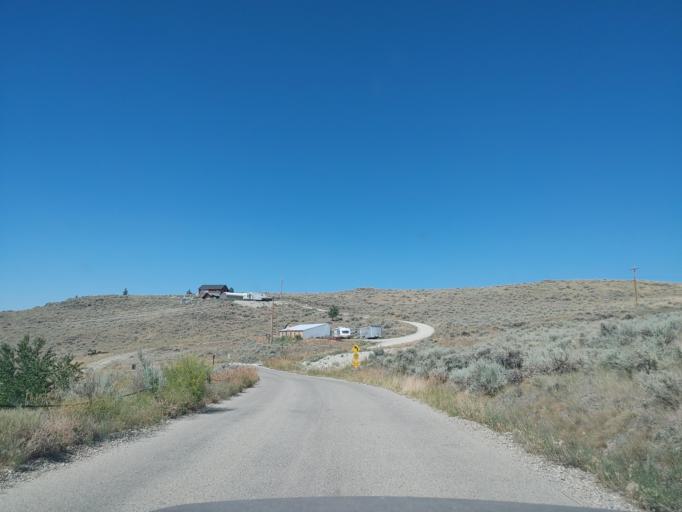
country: US
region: Montana
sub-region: Ravalli County
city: Hamilton
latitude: 46.3495
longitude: -114.0519
